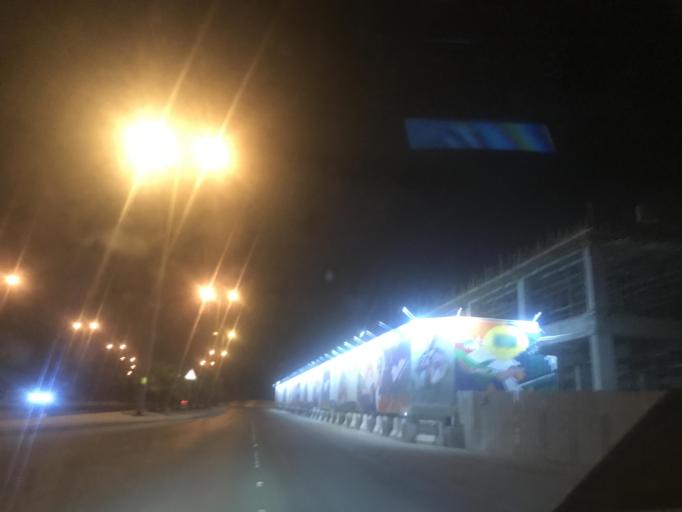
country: SA
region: Ar Riyad
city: Riyadh
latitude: 24.7853
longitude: 46.5912
